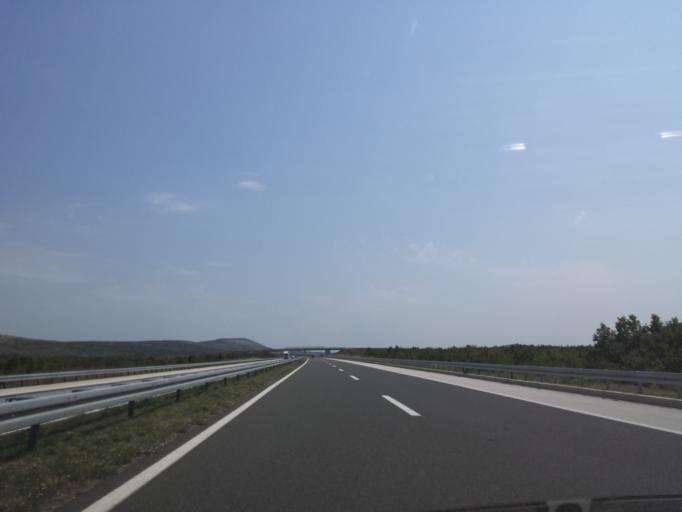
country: HR
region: Zadarska
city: Benkovac
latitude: 43.9580
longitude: 15.6698
